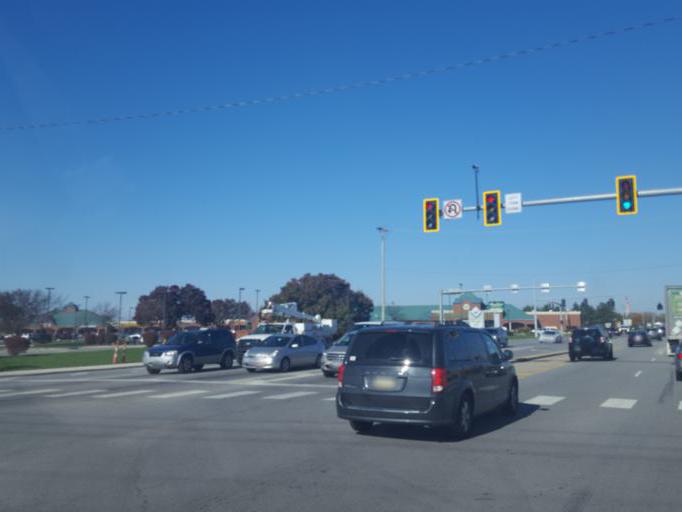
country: US
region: Ohio
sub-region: Wood County
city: Perrysburg
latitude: 41.5366
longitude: -83.6352
